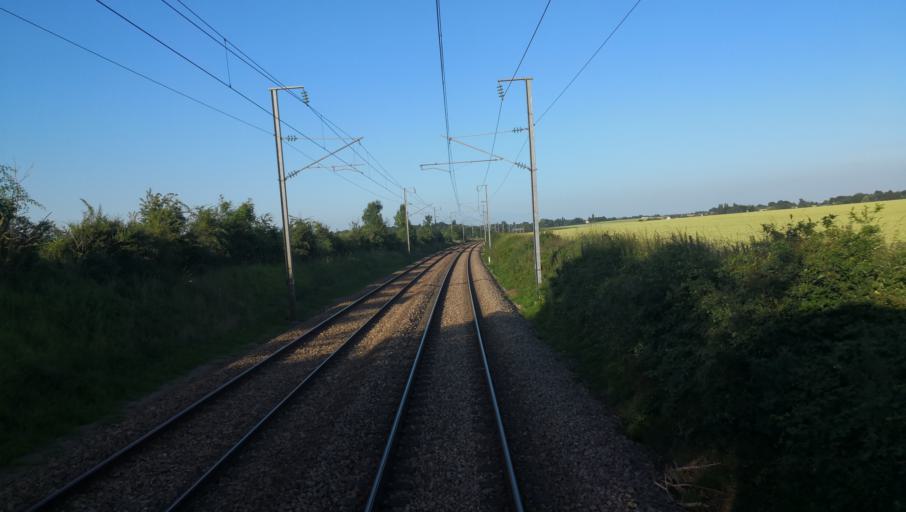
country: FR
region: Haute-Normandie
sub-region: Departement de l'Eure
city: Thiberville
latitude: 49.0803
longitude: 0.4899
